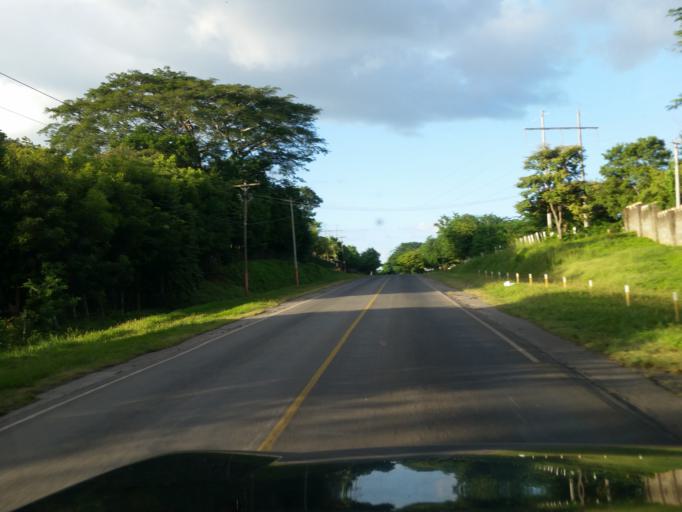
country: NI
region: Granada
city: Nandaime
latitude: 11.7848
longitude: -86.0497
